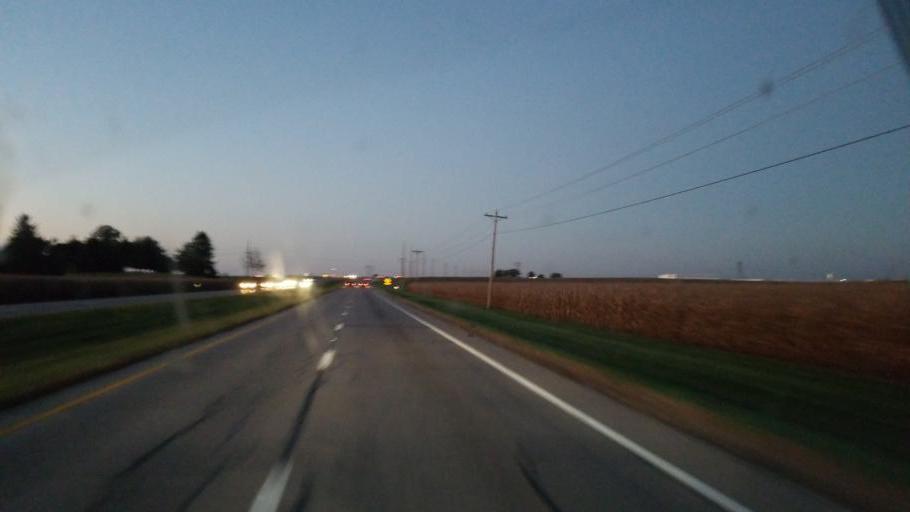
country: US
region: Ohio
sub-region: Pickaway County
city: Logan Elm Village
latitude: 39.5346
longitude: -82.9670
